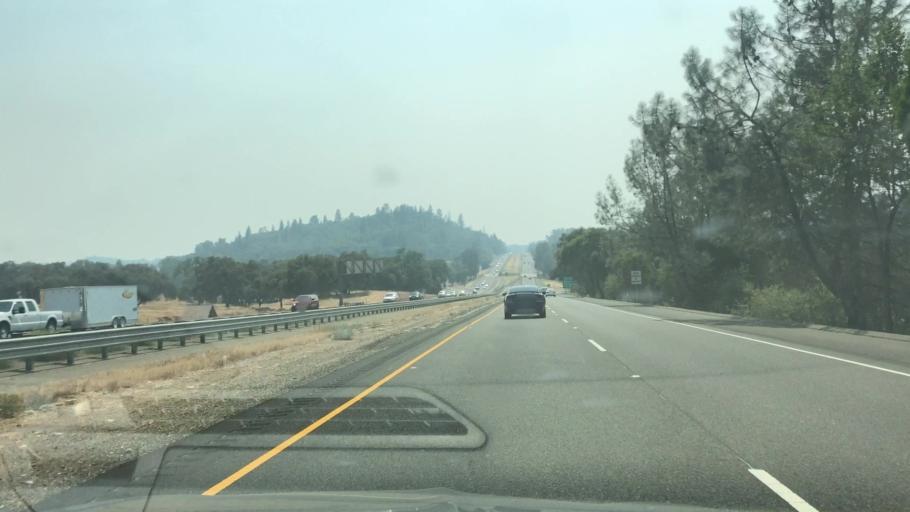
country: US
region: California
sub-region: El Dorado County
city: Shingle Springs
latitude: 38.6850
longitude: -120.9104
